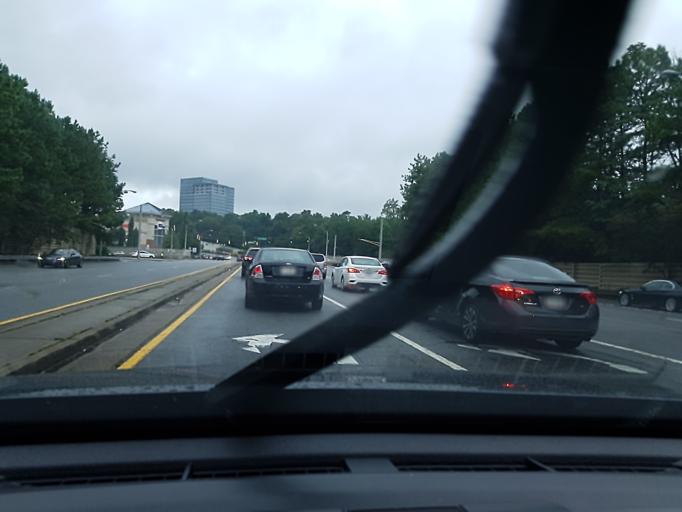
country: US
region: Georgia
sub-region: DeKalb County
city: North Atlanta
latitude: 33.8523
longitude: -84.3683
